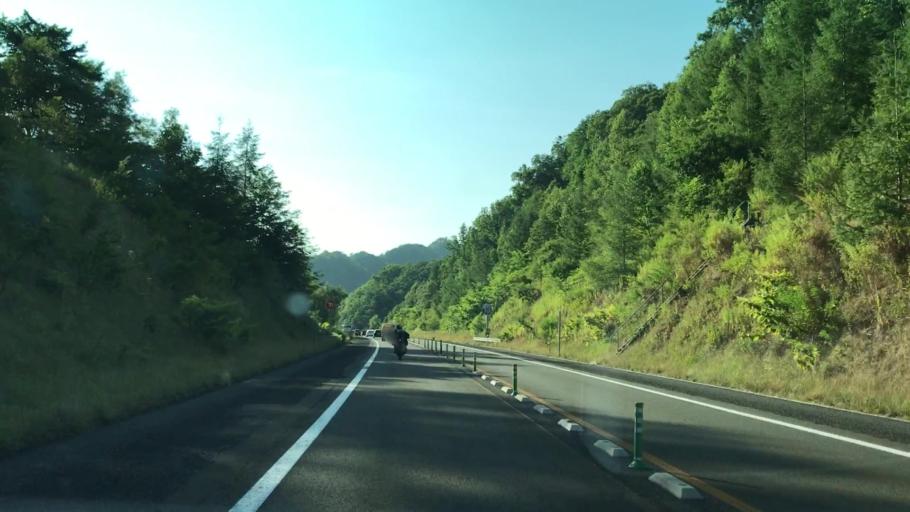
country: JP
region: Hokkaido
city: Chitose
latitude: 42.9120
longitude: 141.9774
